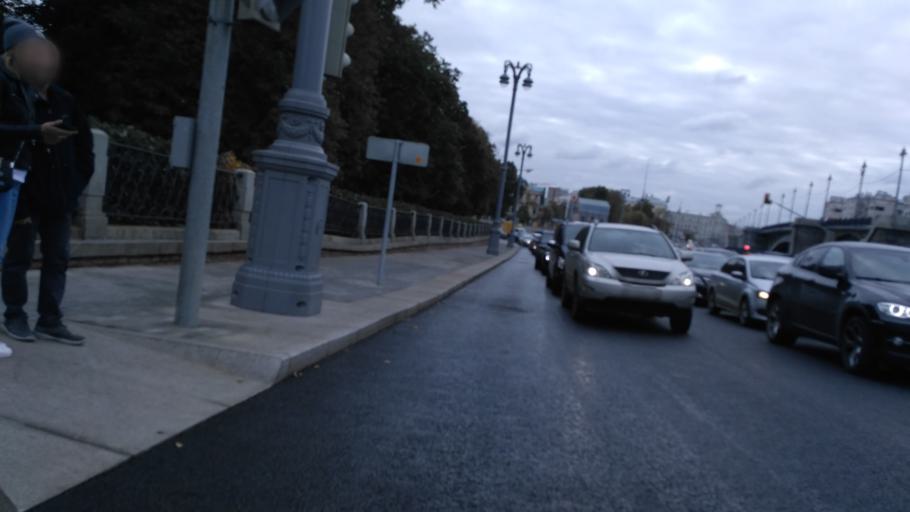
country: RU
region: Moscow
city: Moscow
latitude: 55.7488
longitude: 37.6114
